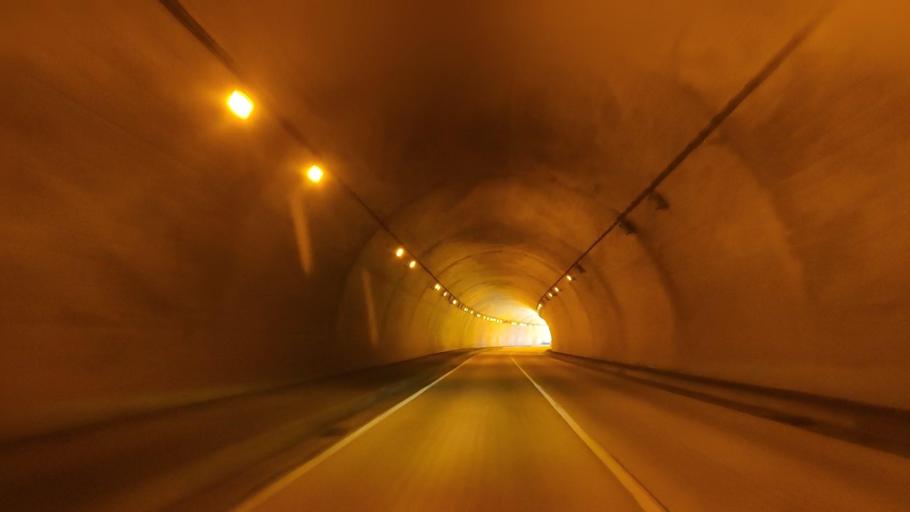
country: JP
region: Ishikawa
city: Nanao
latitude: 37.3831
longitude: 137.2337
